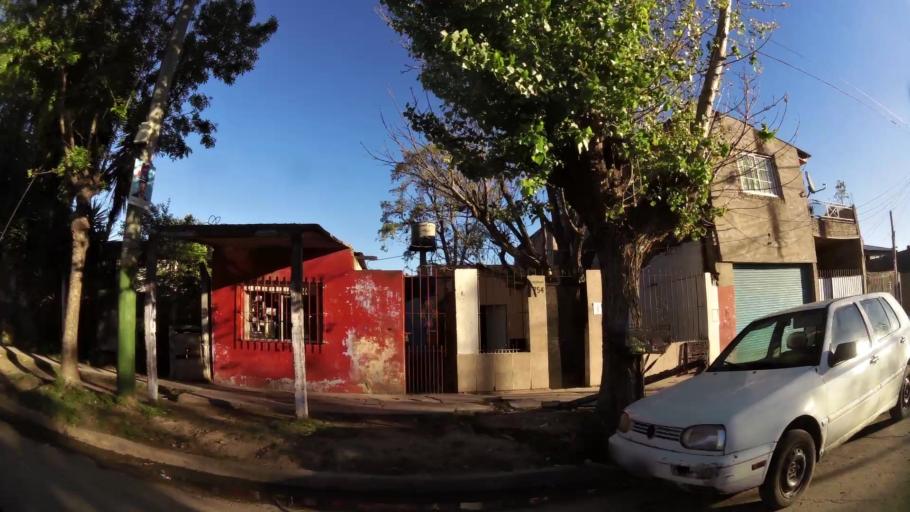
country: AR
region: Buenos Aires
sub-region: Partido de Almirante Brown
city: Adrogue
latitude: -34.7713
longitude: -58.3362
